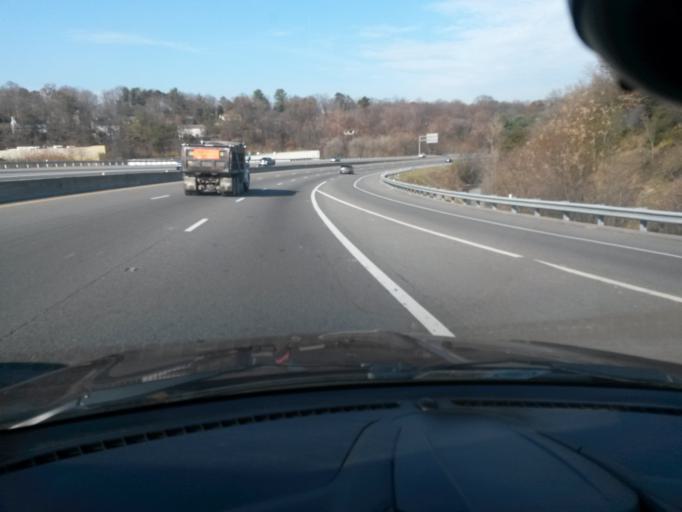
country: US
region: Virginia
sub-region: Roanoke County
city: Narrows
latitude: 37.2334
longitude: -79.9748
